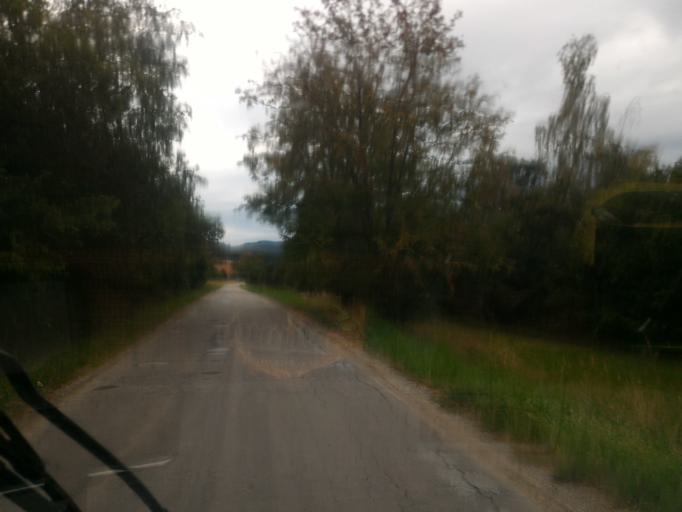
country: CZ
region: Vysocina
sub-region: Okres Jihlava
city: Telc
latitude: 49.1785
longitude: 15.3847
